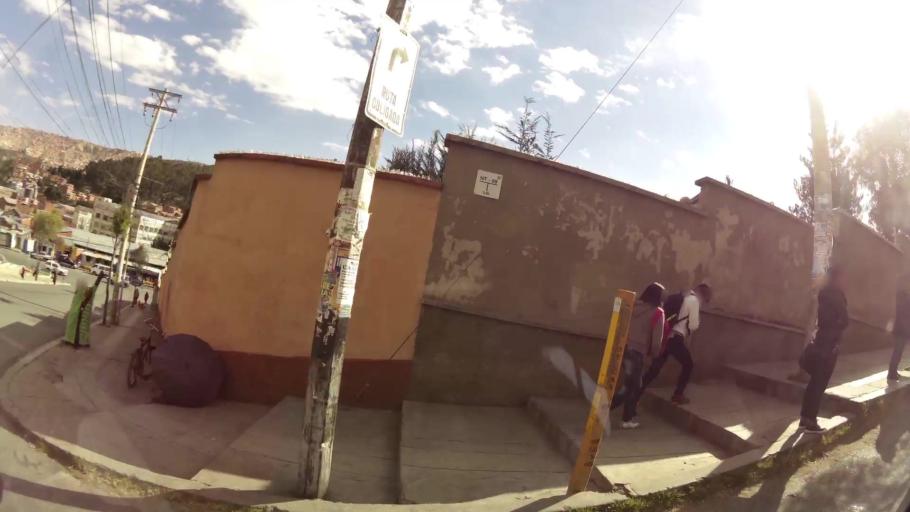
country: BO
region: La Paz
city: La Paz
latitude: -16.4782
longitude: -68.1489
